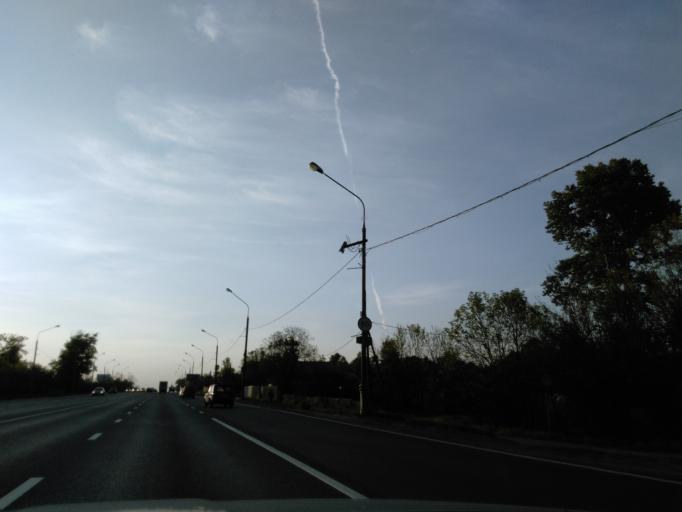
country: RU
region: Moscow
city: Khimki
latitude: 55.9224
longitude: 37.3903
